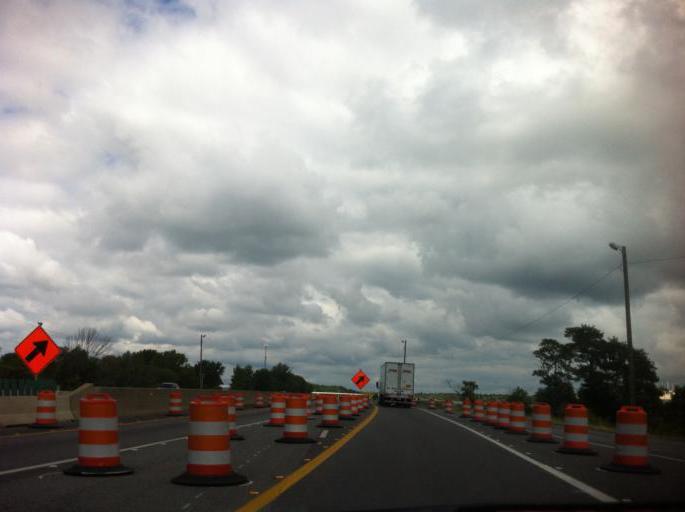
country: US
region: Ohio
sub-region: Trumbull County
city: Lordstown
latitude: 41.1422
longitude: -80.8780
